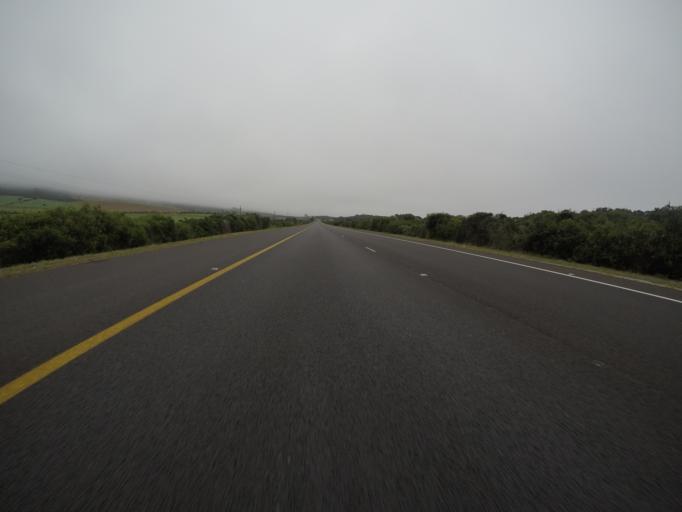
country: ZA
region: Western Cape
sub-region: Eden District Municipality
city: Mossel Bay
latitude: -34.0649
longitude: 22.1764
